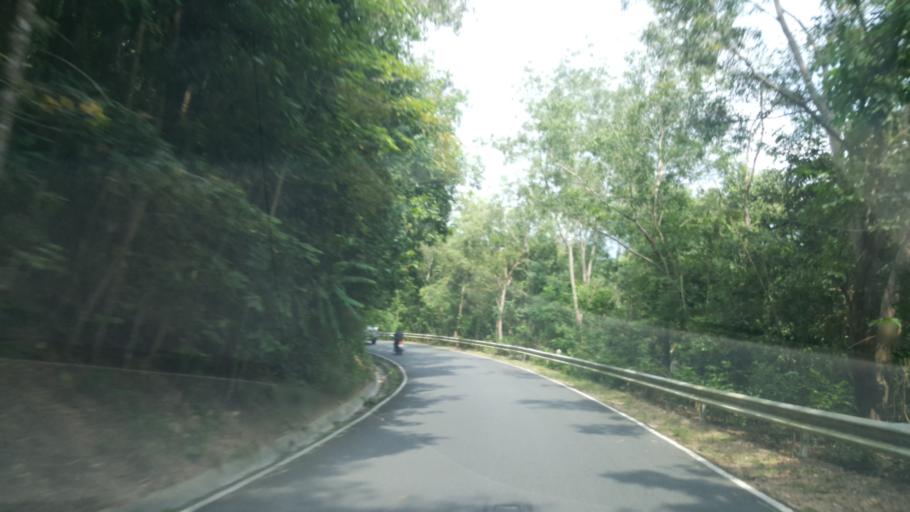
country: TH
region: Chon Buri
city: Ban Bueng
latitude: 13.2085
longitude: 101.0568
